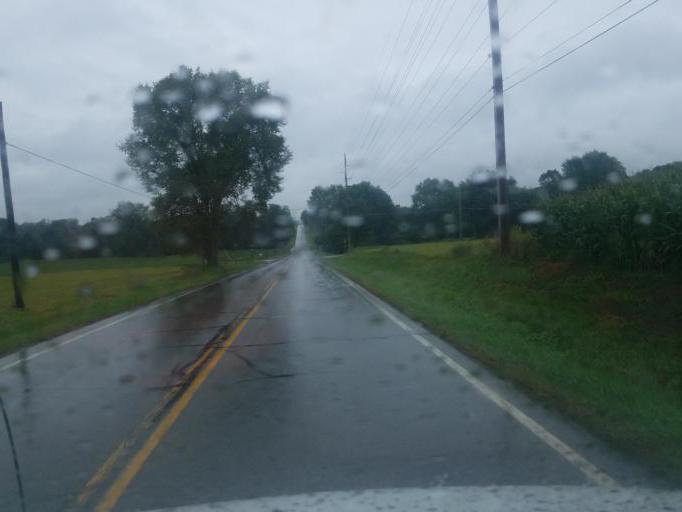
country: US
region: Ohio
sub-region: Medina County
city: Seville
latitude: 41.0252
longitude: -81.8482
